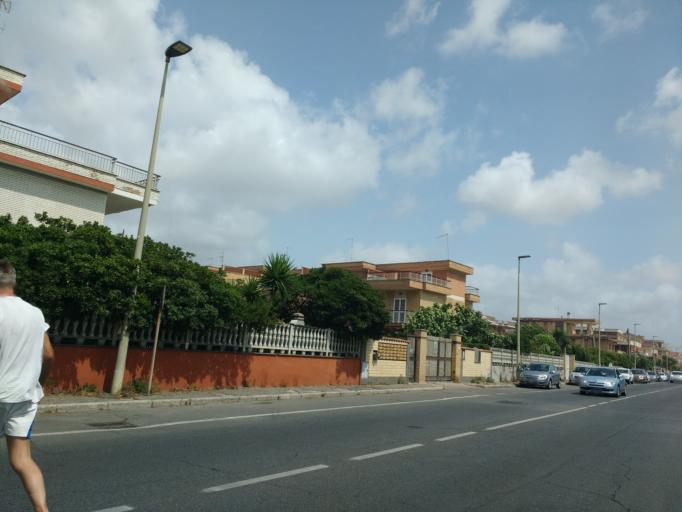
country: IT
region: Latium
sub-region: Citta metropolitana di Roma Capitale
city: Torvaianica
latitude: 41.6467
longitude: 12.4307
